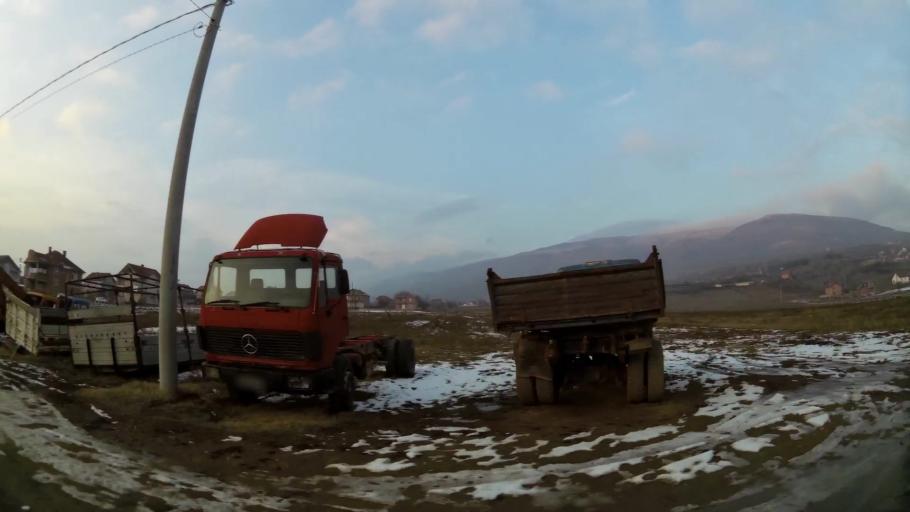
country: MK
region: Aracinovo
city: Arachinovo
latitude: 42.0266
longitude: 21.5503
